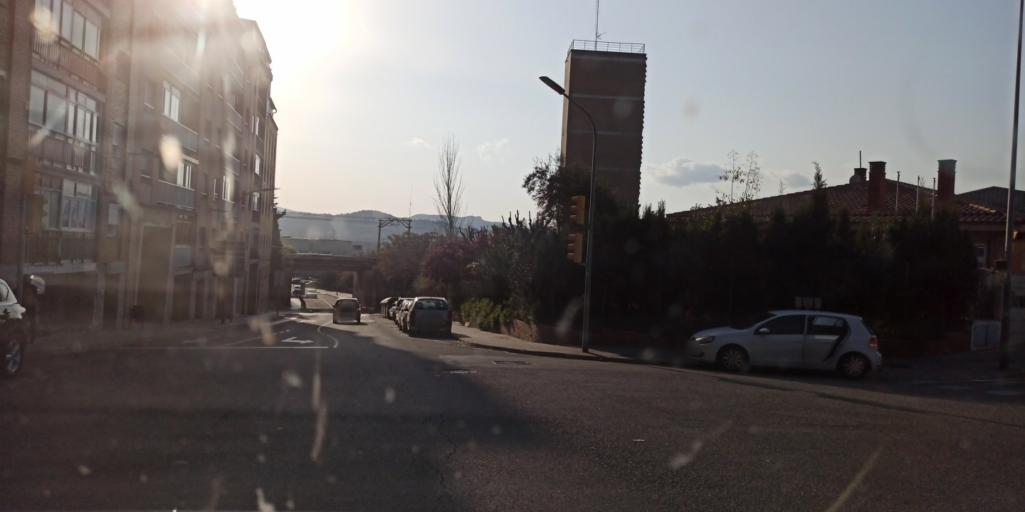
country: ES
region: Catalonia
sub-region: Provincia de Barcelona
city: Sant Feliu de Llobregat
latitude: 41.3883
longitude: 2.0437
